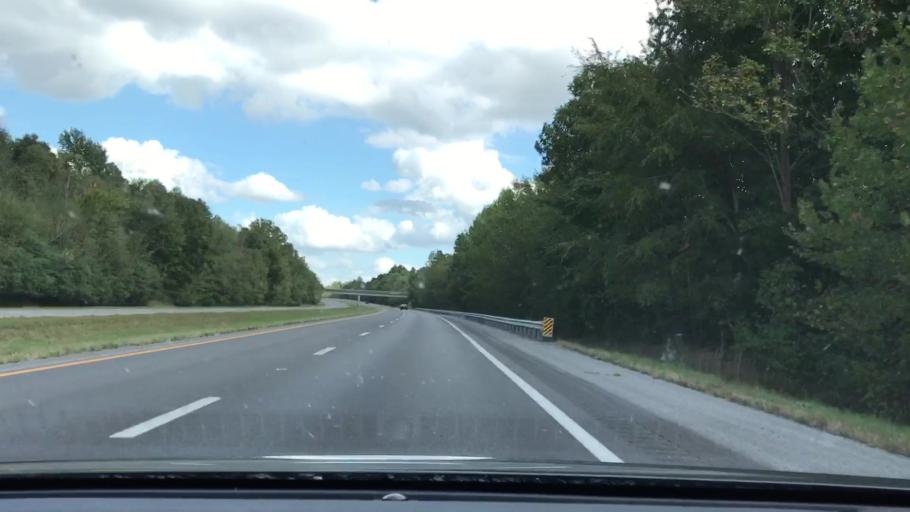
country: US
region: Kentucky
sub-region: Graves County
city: Mayfield
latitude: 36.7698
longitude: -88.6153
